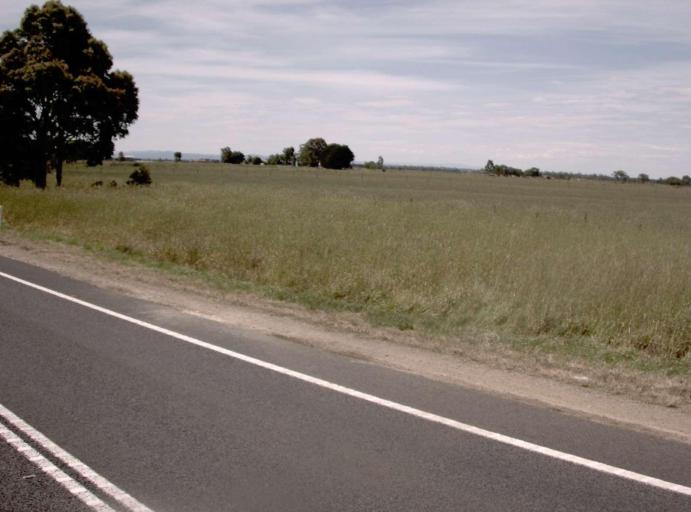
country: AU
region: Victoria
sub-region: Wellington
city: Sale
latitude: -38.0596
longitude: 147.0701
